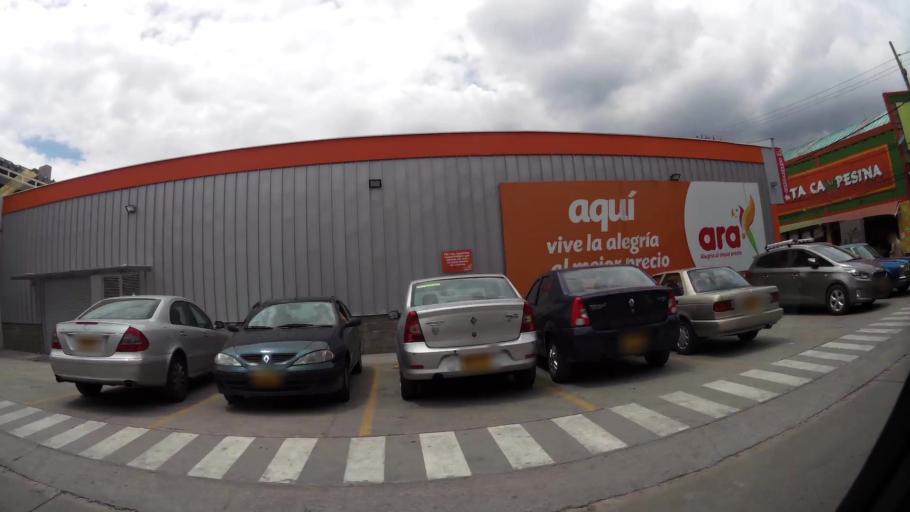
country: CO
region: Cundinamarca
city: La Calera
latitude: 4.7629
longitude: -74.0299
